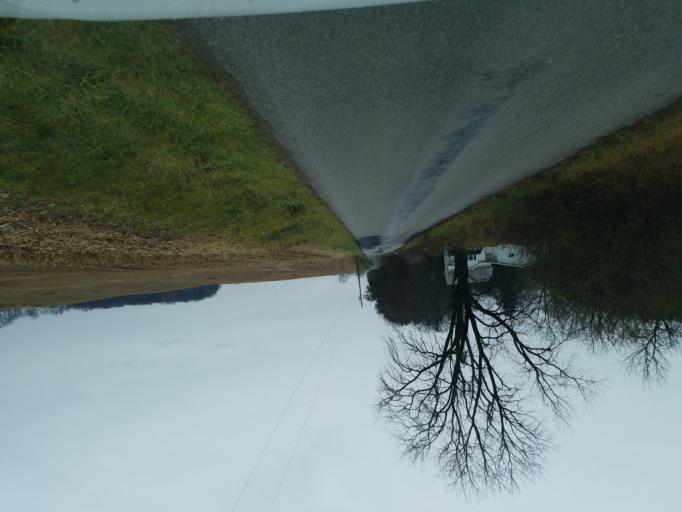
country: US
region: Ohio
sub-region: Knox County
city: Fredericktown
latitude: 40.5066
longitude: -82.5711
